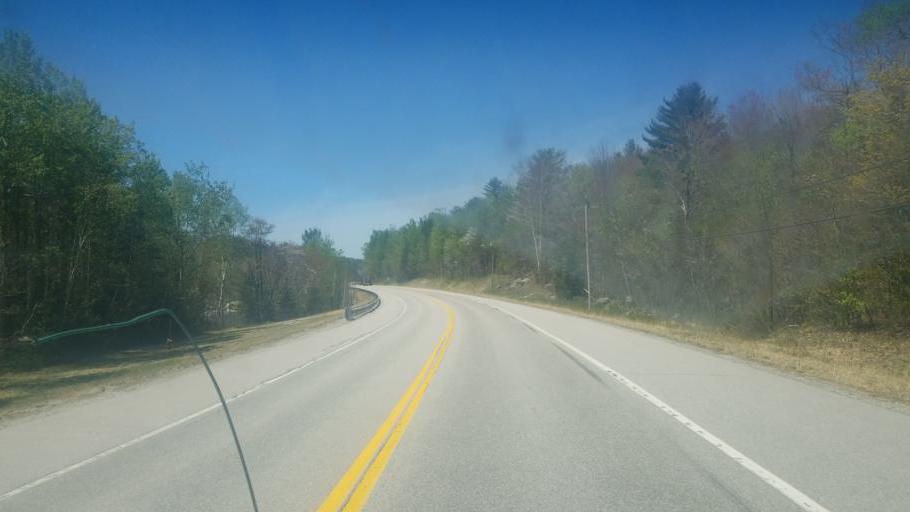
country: US
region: New Hampshire
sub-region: Grafton County
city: Deerfield
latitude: 44.2690
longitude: -71.5300
